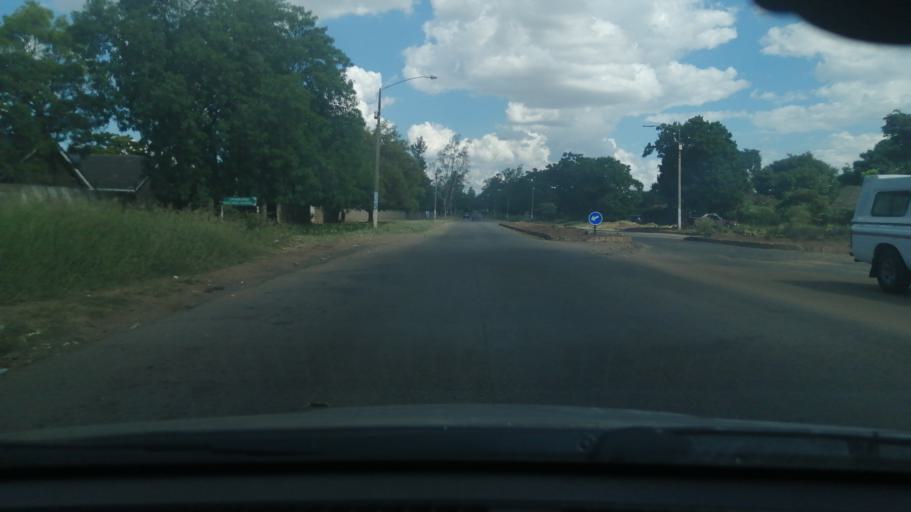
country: ZW
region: Harare
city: Harare
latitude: -17.8495
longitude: 31.0813
